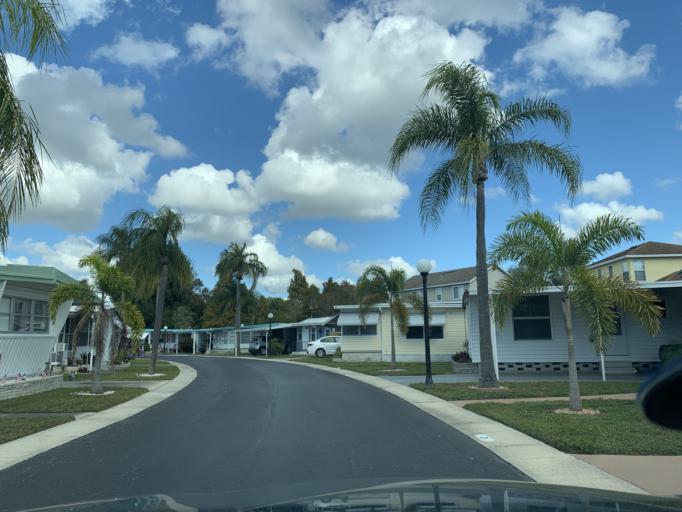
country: US
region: Florida
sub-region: Pinellas County
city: Kenneth City
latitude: 27.8087
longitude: -82.7480
